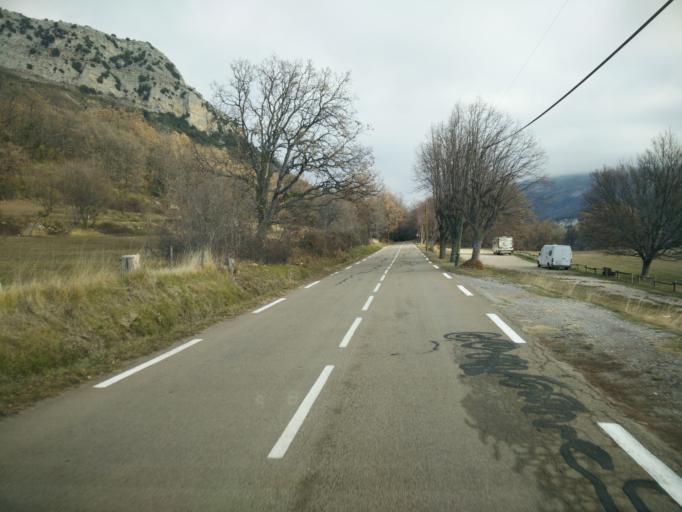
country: FR
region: Provence-Alpes-Cote d'Azur
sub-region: Departement des Alpes-Maritimes
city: Opio
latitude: 43.7233
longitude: 6.9806
